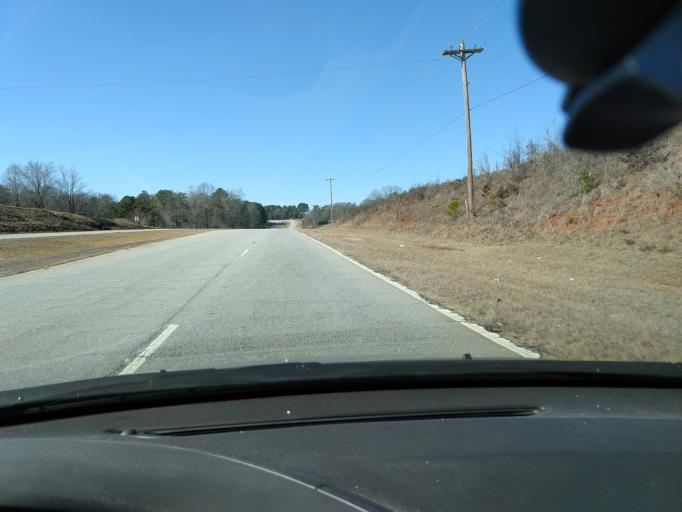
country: US
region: South Carolina
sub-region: Oconee County
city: Westminster
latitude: 34.6659
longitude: -83.0596
